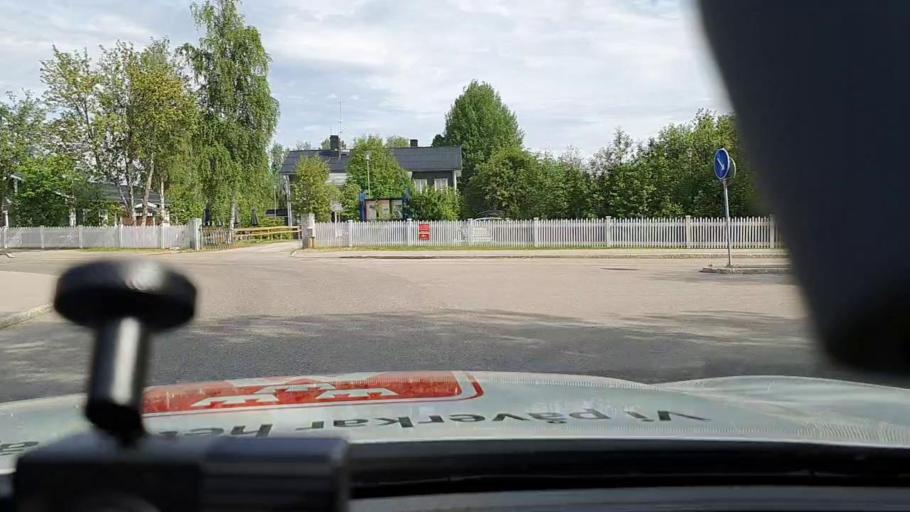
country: SE
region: Norrbotten
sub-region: Jokkmokks Kommun
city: Jokkmokk
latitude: 66.6059
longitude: 19.8339
